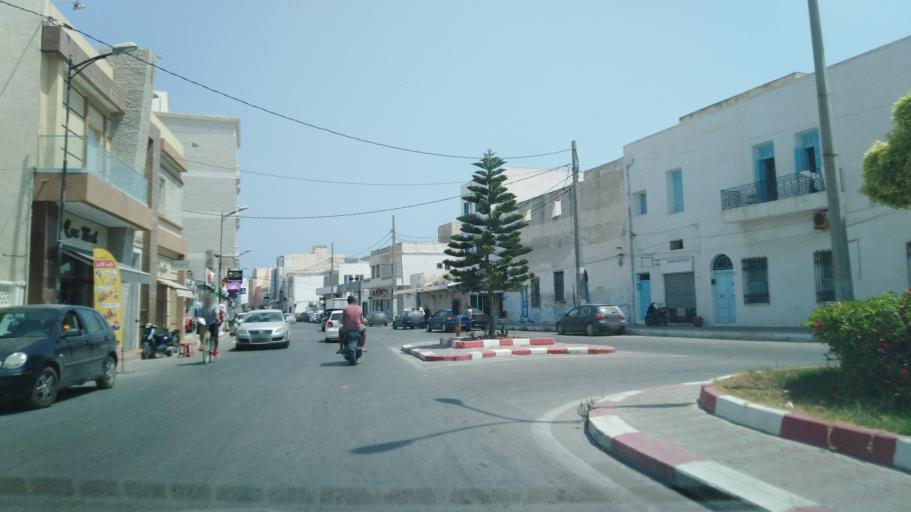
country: TN
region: Al Mahdiyah
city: Mahdia
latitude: 35.5053
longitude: 11.0624
